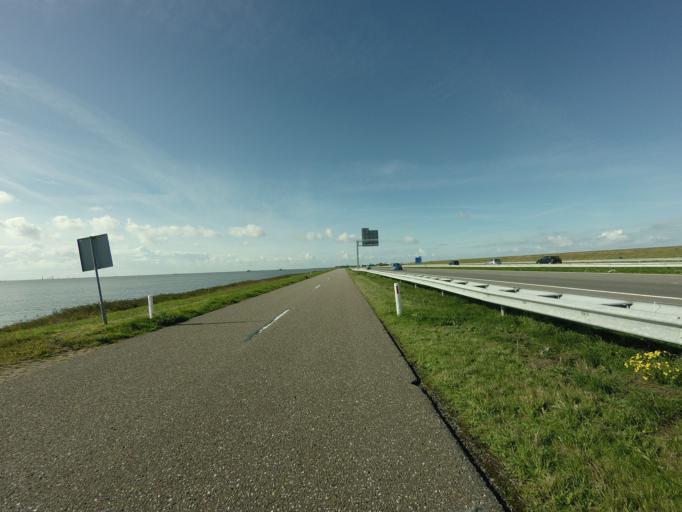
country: NL
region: Friesland
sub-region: Sudwest Fryslan
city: Makkum
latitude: 53.0794
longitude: 5.3539
